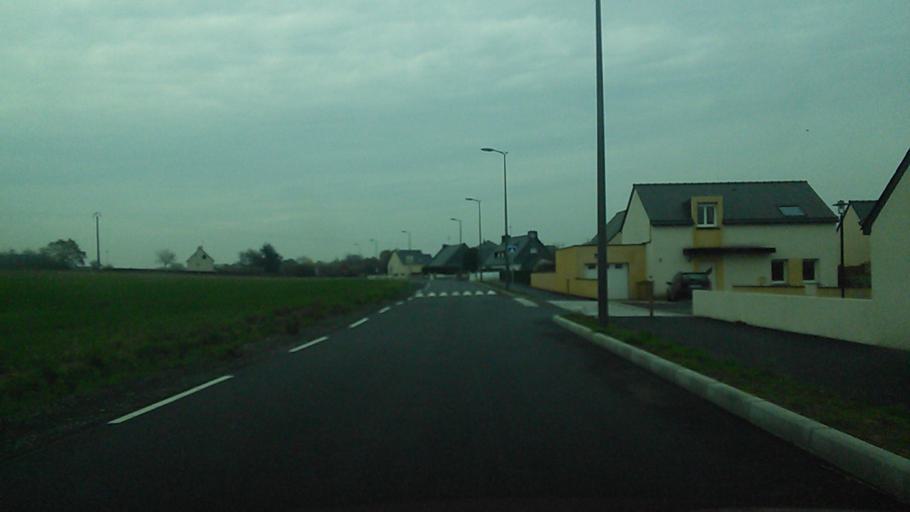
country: FR
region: Brittany
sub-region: Departement des Cotes-d'Armor
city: Yffiniac
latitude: 48.4825
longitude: -2.6599
